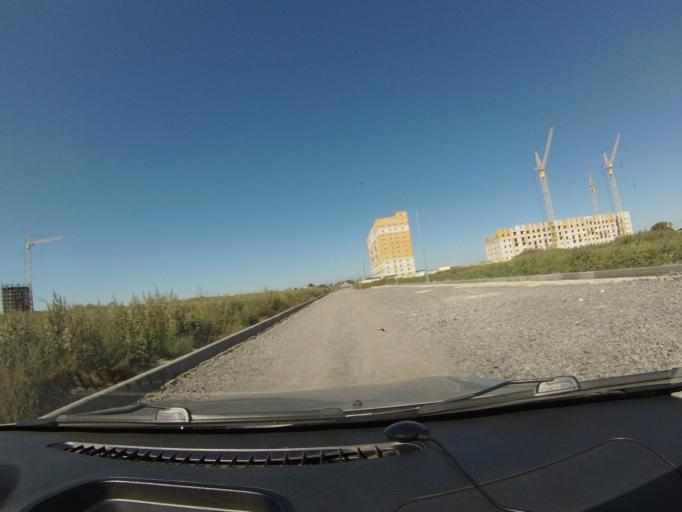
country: RU
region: Tambov
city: Tambov
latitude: 52.7770
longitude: 41.4078
